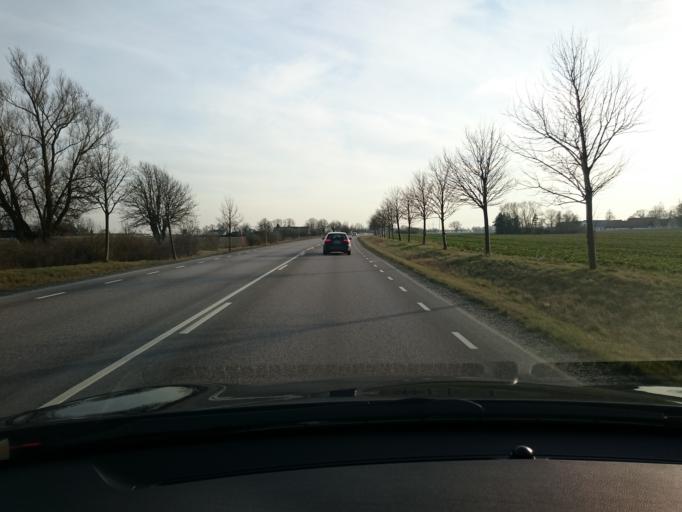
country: SE
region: Skane
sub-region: Staffanstorps Kommun
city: Hjaerup
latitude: 55.6745
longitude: 13.1675
